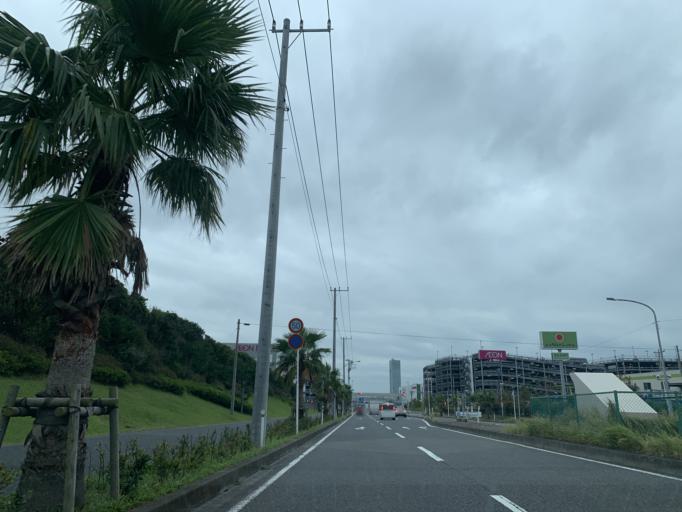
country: JP
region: Chiba
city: Funabashi
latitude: 35.6586
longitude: 140.0231
